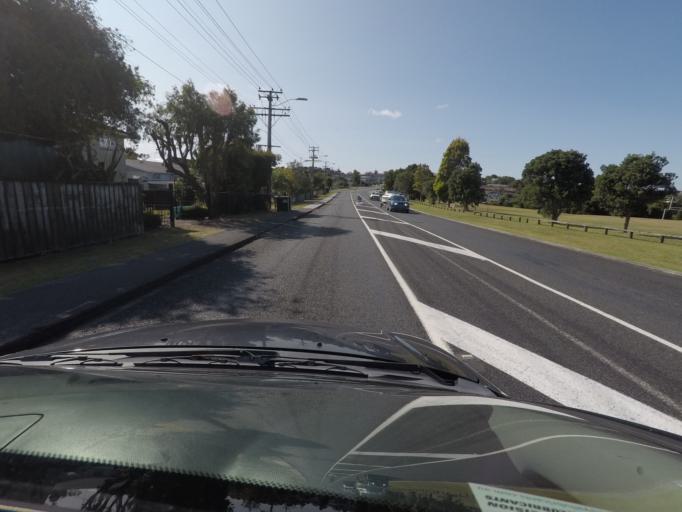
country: NZ
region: Auckland
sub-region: Auckland
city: Warkworth
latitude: -36.4219
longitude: 174.7254
